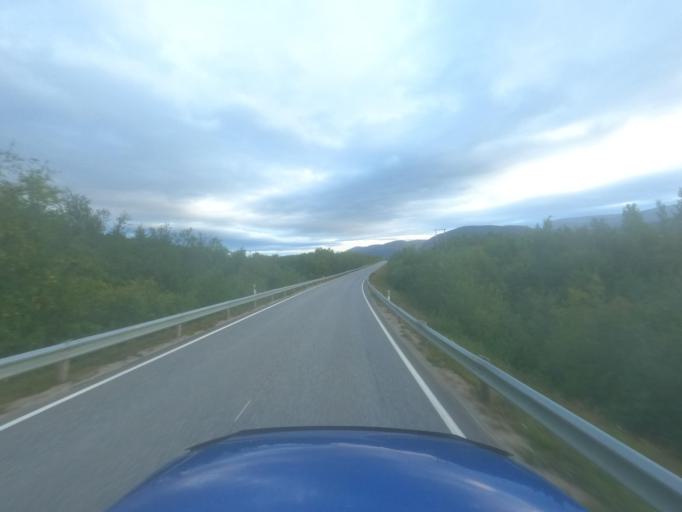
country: NO
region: Finnmark Fylke
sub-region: Porsanger
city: Lakselv
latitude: 70.0111
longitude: 24.9650
